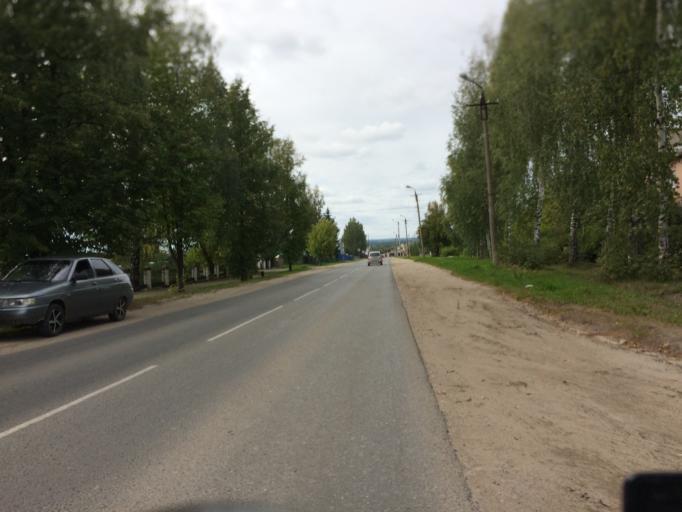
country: RU
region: Mariy-El
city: Yoshkar-Ola
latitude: 56.6554
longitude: 47.9759
